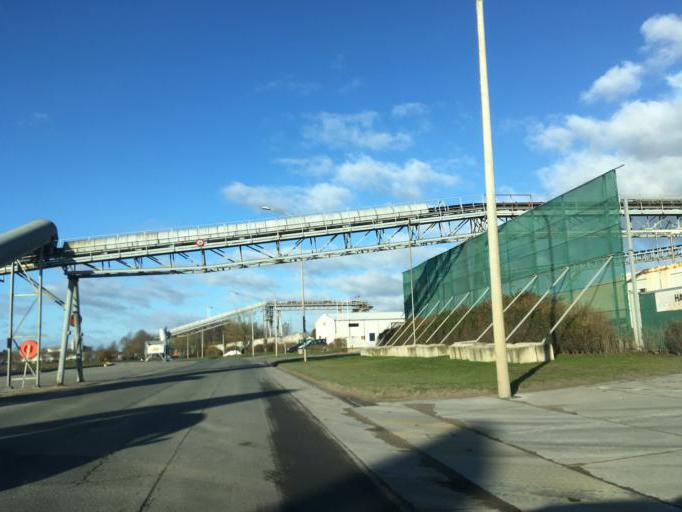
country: BE
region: Flanders
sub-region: Provincie West-Vlaanderen
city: Roeselare
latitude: 50.9436
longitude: 3.1576
